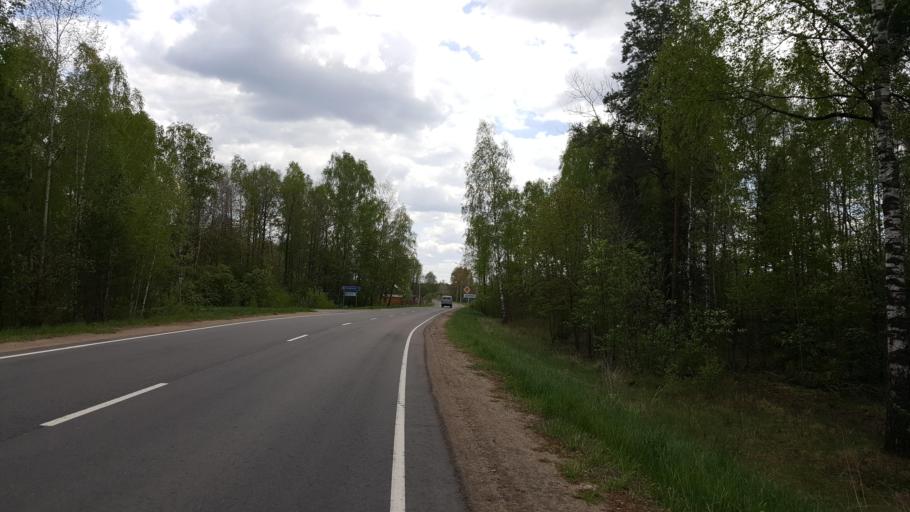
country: BY
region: Brest
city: Zhabinka
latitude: 52.3975
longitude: 24.0886
